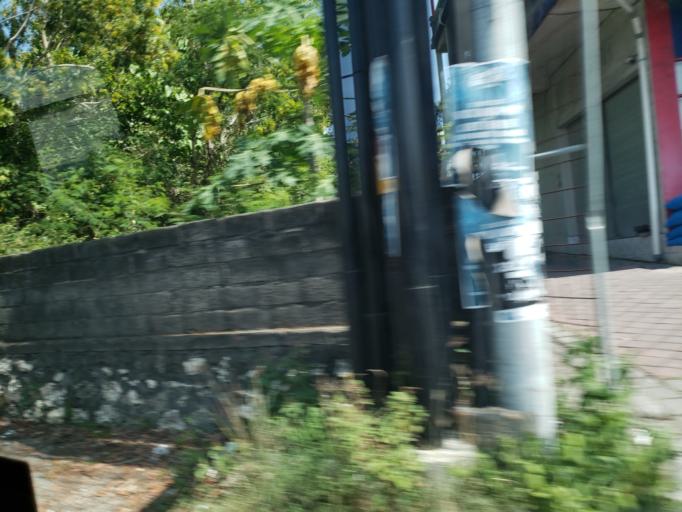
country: ID
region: Bali
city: Kangin
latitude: -8.8286
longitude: 115.1382
